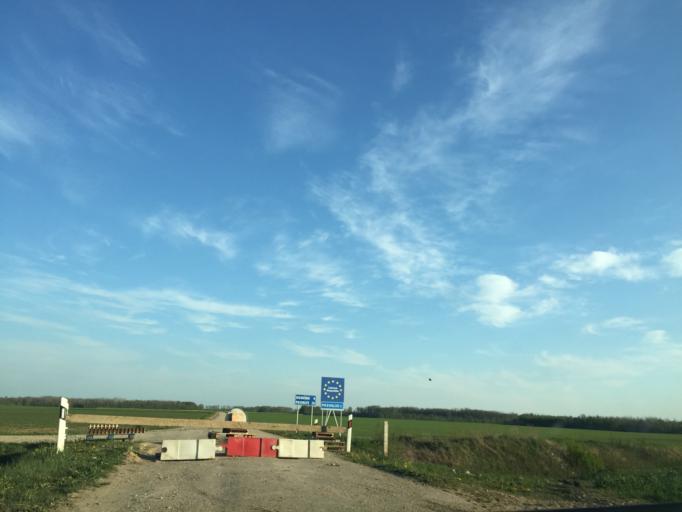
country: LV
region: Bauskas Rajons
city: Bauska
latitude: 56.2813
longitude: 24.2655
